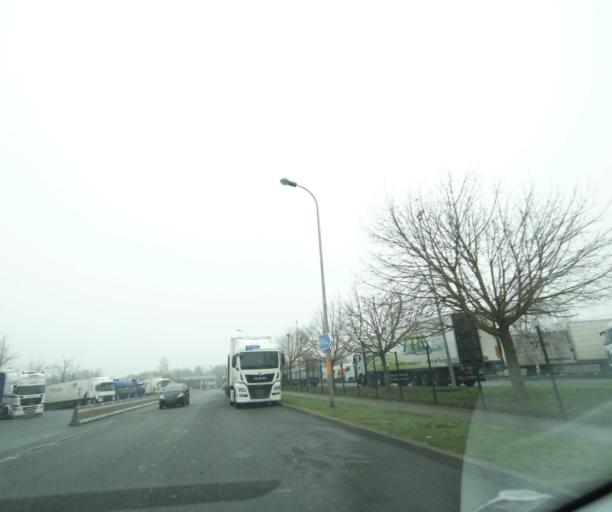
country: FR
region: Ile-de-France
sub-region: Departement de Seine-et-Marne
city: Dammartin-en-Goele
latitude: 49.0639
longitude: 2.6979
